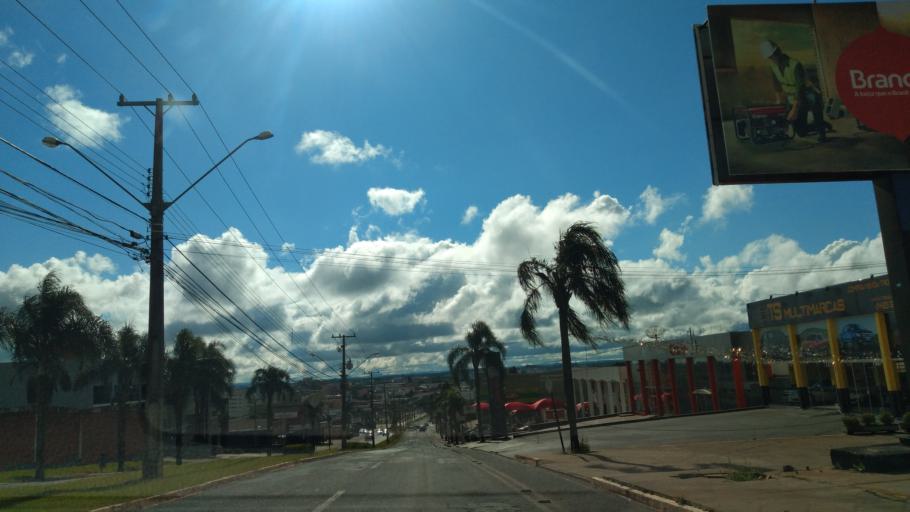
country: BR
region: Parana
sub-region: Guarapuava
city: Guarapuava
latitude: -25.3813
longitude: -51.4693
